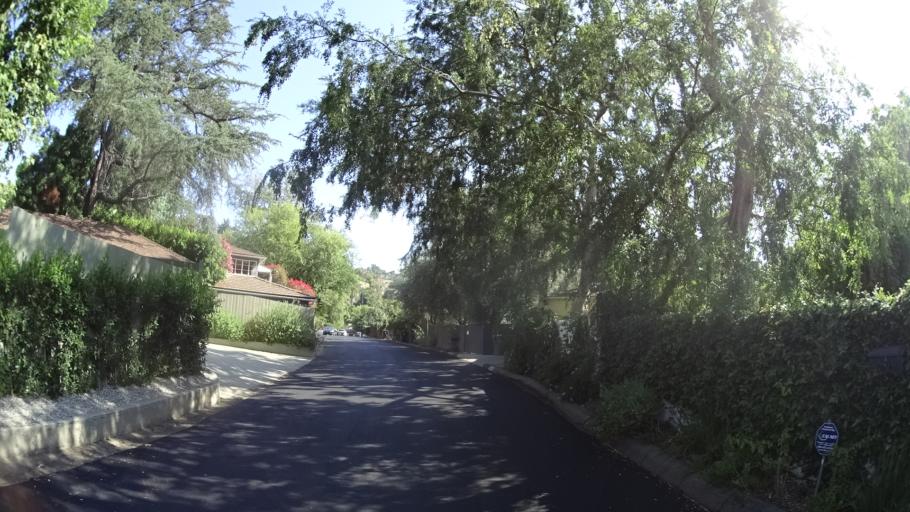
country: US
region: California
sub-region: Los Angeles County
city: Universal City
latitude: 34.1409
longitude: -118.3745
